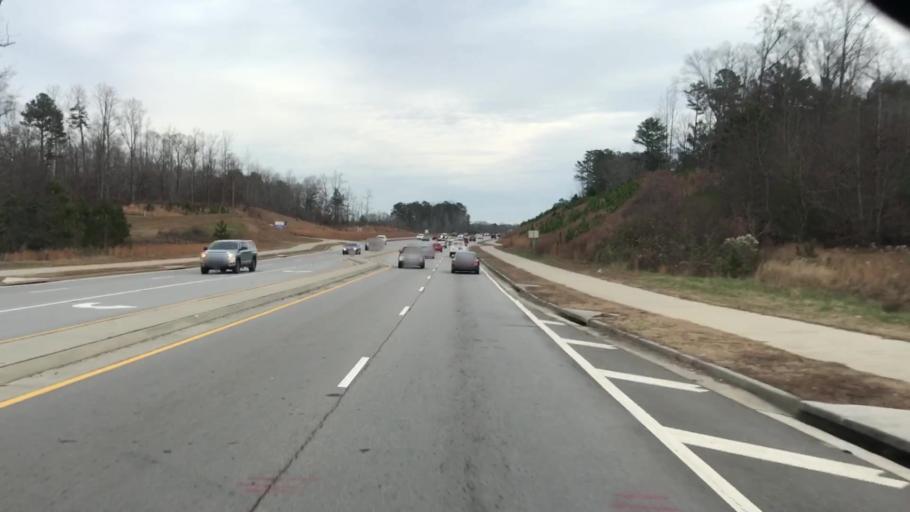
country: US
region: Georgia
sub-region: Hall County
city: Flowery Branch
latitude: 34.1097
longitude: -83.8716
